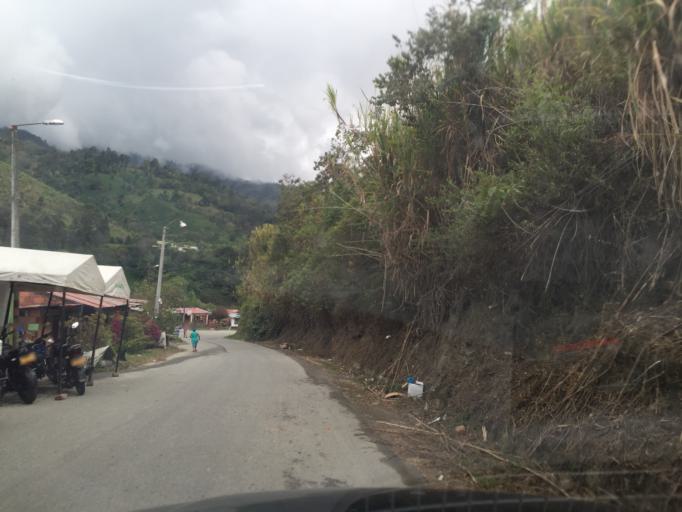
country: CO
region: Tolima
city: Cajamarca
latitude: 4.4237
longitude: -75.4319
